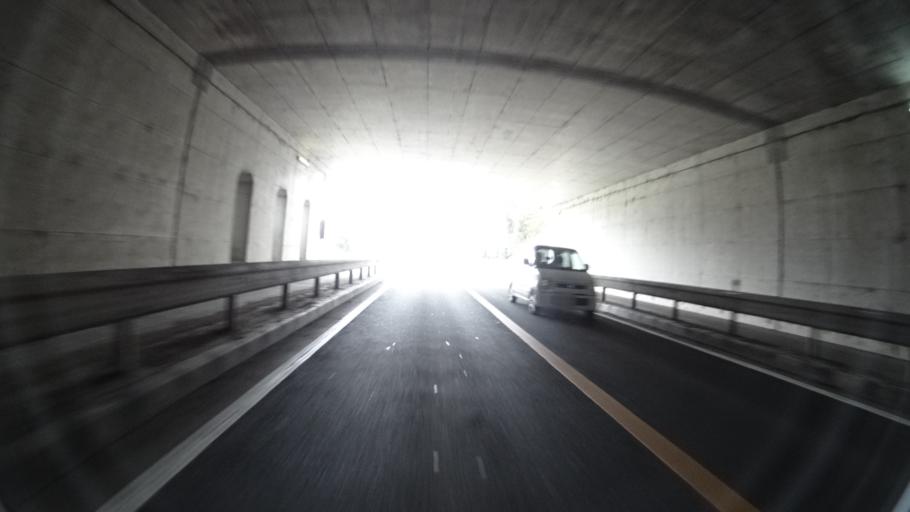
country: JP
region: Hyogo
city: Sasayama
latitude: 35.1454
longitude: 135.1261
